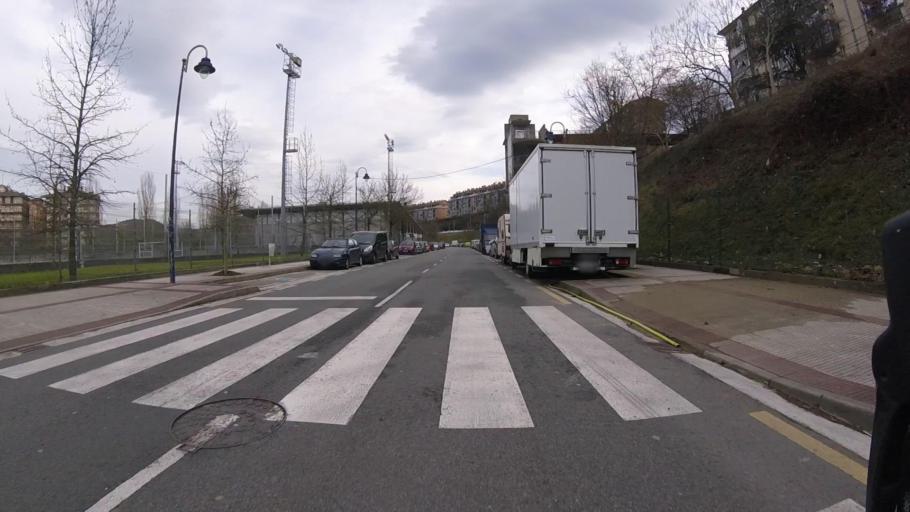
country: ES
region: Basque Country
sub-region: Provincia de Guipuzcoa
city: Errenteria
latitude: 43.3095
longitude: -1.8937
